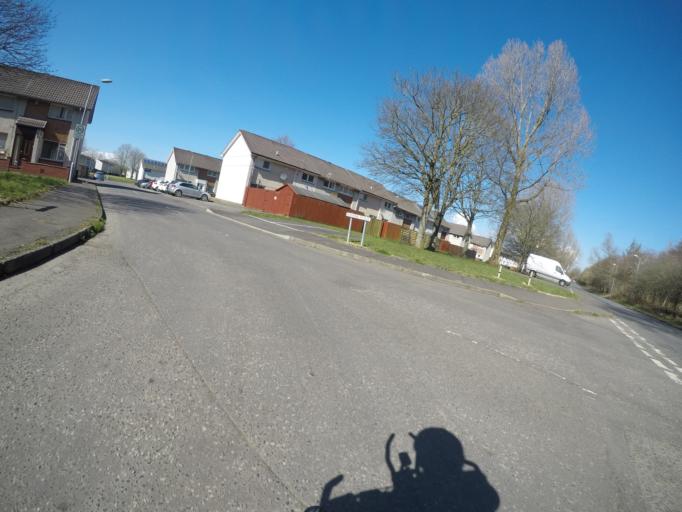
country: GB
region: Scotland
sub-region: North Ayrshire
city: Irvine
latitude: 55.6297
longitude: -4.6580
